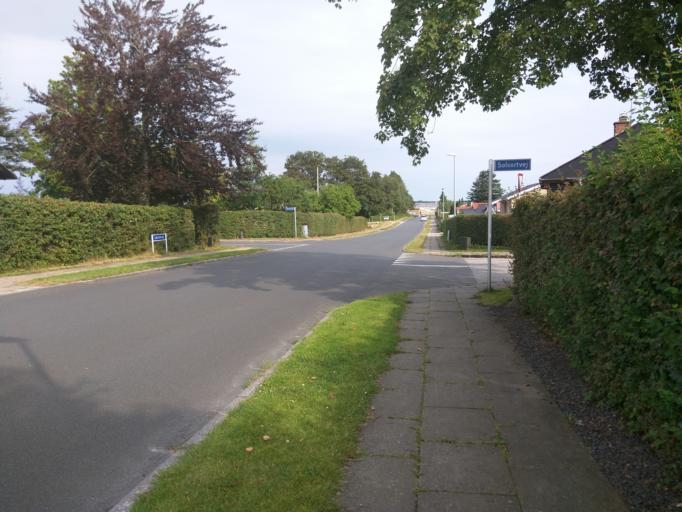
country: DK
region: Central Jutland
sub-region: Viborg Kommune
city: Viborg
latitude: 56.4451
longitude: 9.3838
